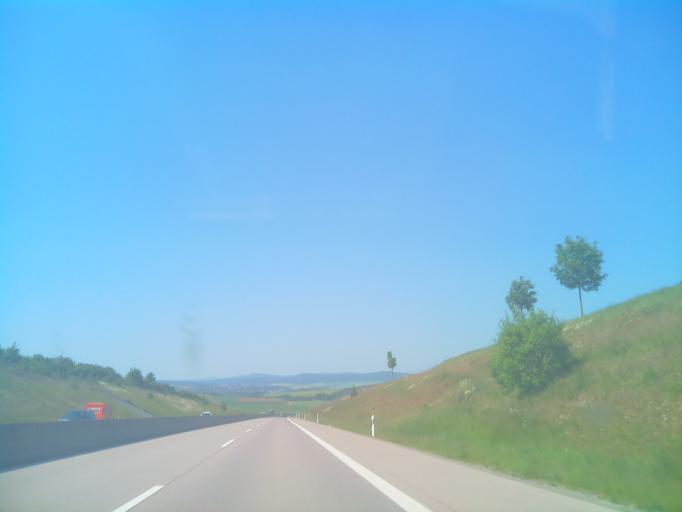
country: DE
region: Bavaria
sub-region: Regierungsbezirk Unterfranken
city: Hollstadt
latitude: 50.3719
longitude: 10.3148
